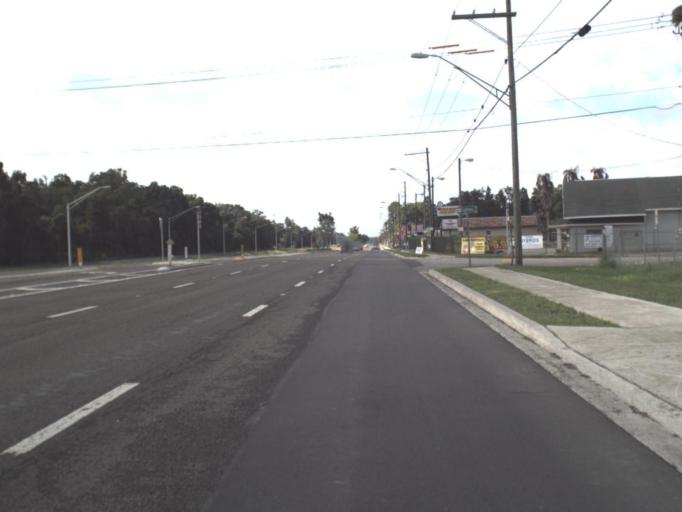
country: US
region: Florida
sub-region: Hillsborough County
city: Lutz
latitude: 28.1283
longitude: -82.4636
